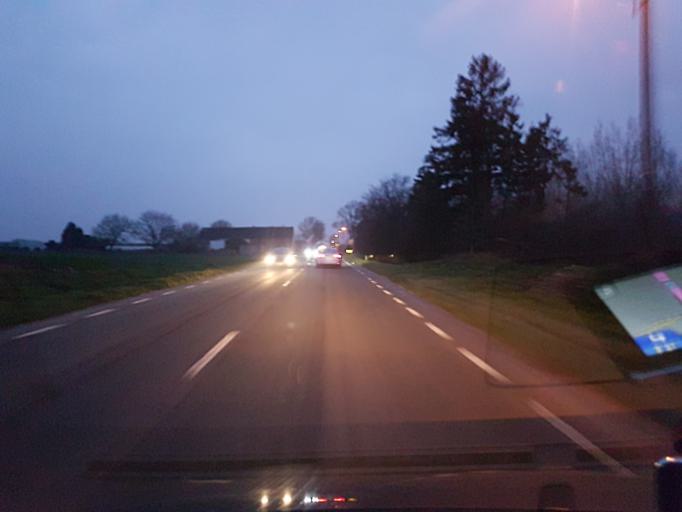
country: BE
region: Wallonia
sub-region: Province du Brabant Wallon
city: Ramillies
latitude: 50.6193
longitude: 4.8820
